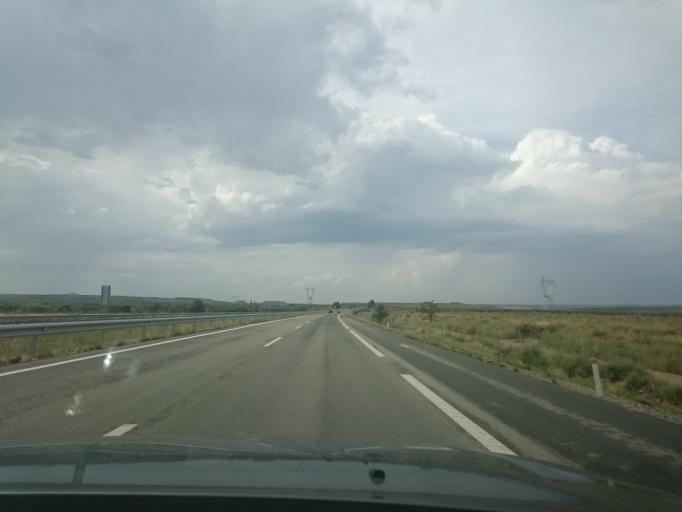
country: ES
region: La Rioja
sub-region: Provincia de La Rioja
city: Rincon de Soto
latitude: 42.1713
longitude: -1.8325
